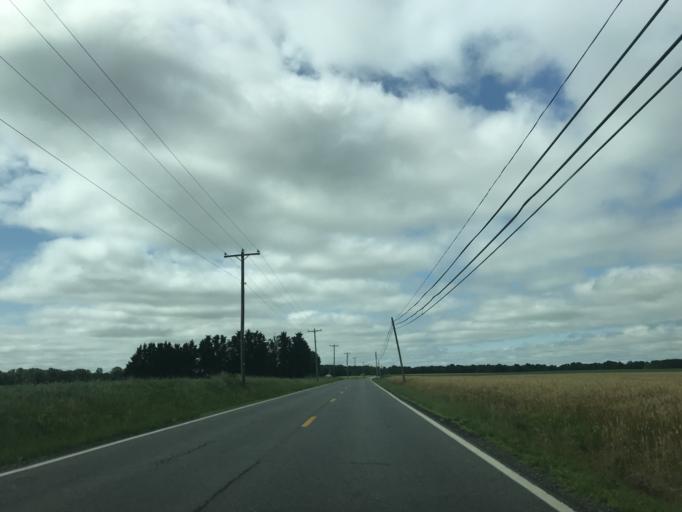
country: US
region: Maryland
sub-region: Caroline County
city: Ridgely
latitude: 38.9036
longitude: -75.9584
